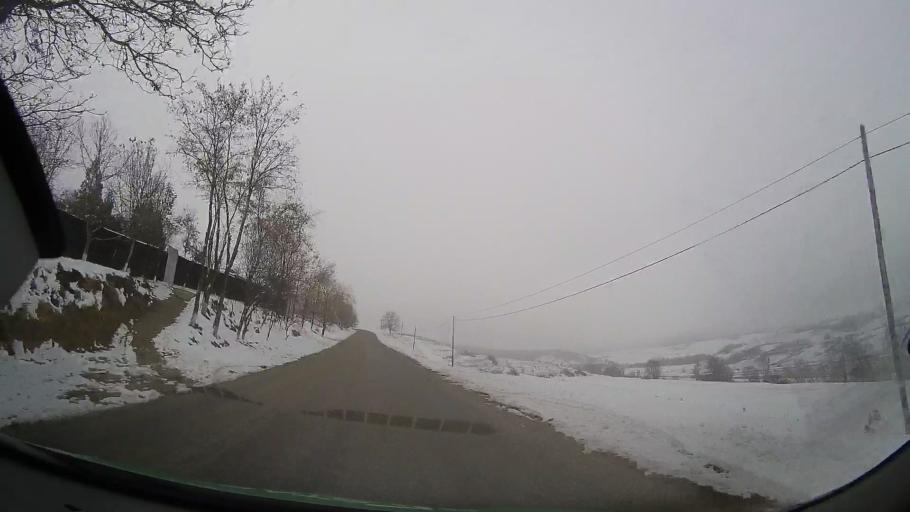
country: RO
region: Bacau
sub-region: Comuna Vultureni
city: Vultureni
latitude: 46.3787
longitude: 27.2757
